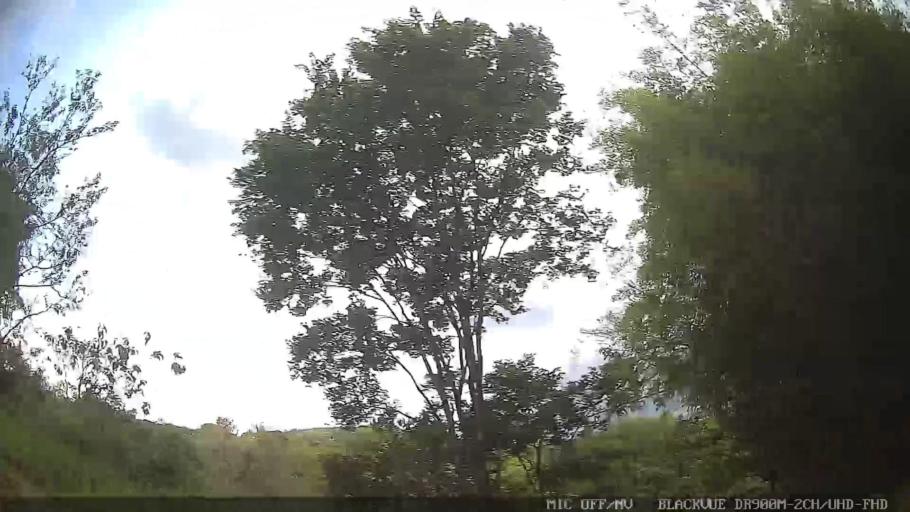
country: BR
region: Sao Paulo
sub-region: Itatiba
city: Itatiba
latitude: -22.8591
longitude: -46.7882
